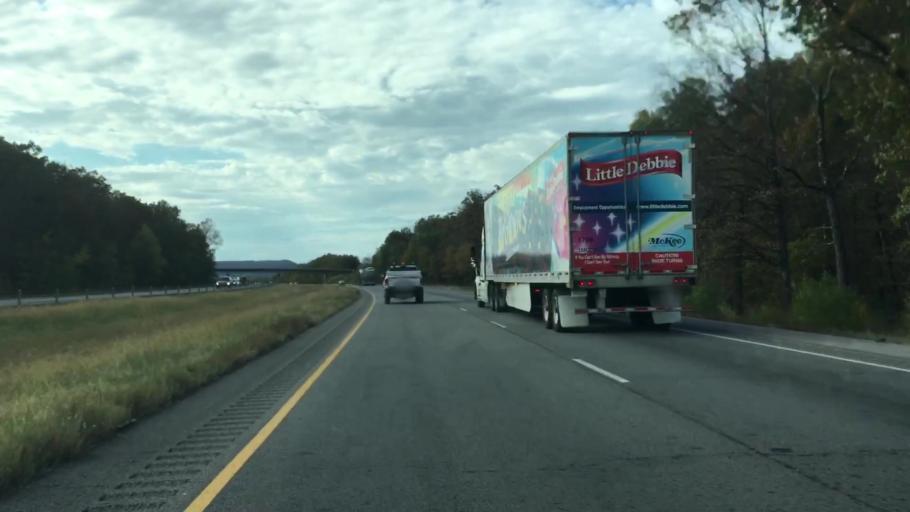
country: US
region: Arkansas
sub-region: Pope County
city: Atkins
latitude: 35.2467
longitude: -92.8681
